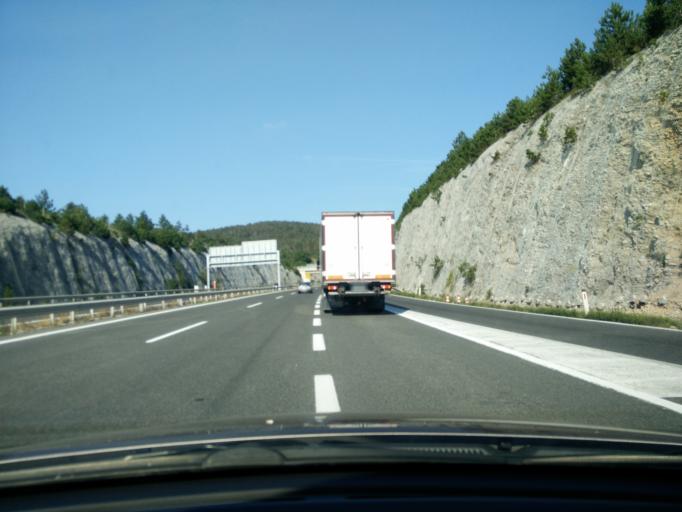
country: SI
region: Divaca
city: Divaca
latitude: 45.6976
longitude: 13.9825
